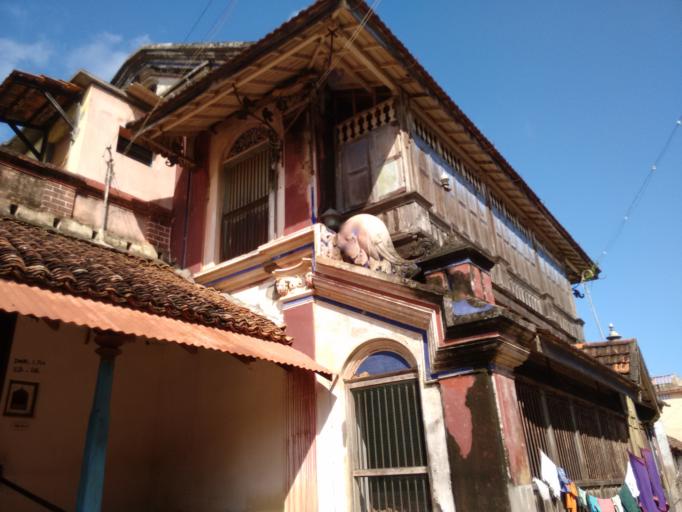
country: IN
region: Tamil Nadu
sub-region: Thiruvarur
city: Koradachcheri
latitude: 10.8502
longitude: 79.5107
